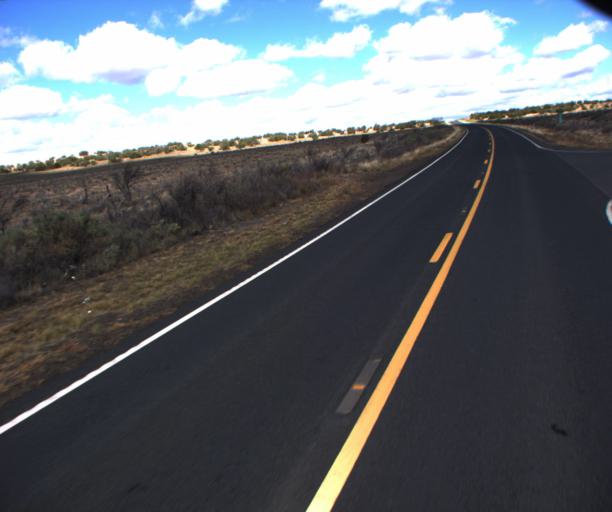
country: US
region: Arizona
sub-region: Apache County
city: Houck
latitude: 35.0970
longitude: -109.3125
